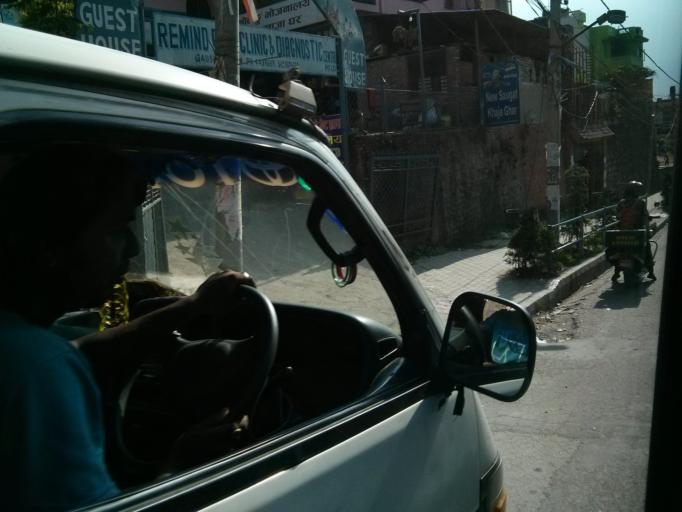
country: NP
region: Central Region
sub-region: Bagmati Zone
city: Kathmandu
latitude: 27.7078
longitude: 85.3432
